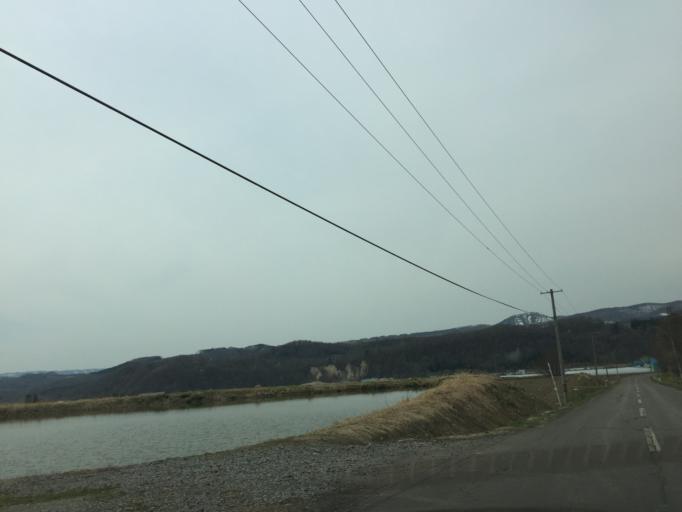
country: JP
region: Hokkaido
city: Ashibetsu
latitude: 43.6078
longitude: 142.2151
